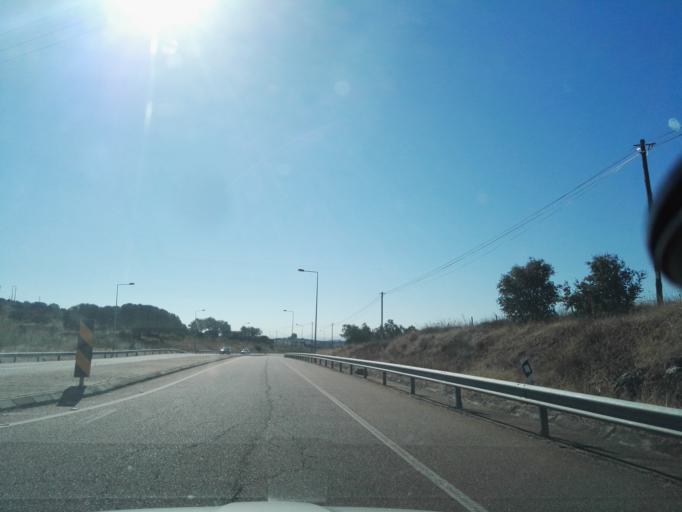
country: PT
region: Portalegre
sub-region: Elvas
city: Elvas
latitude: 38.9070
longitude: -7.1794
